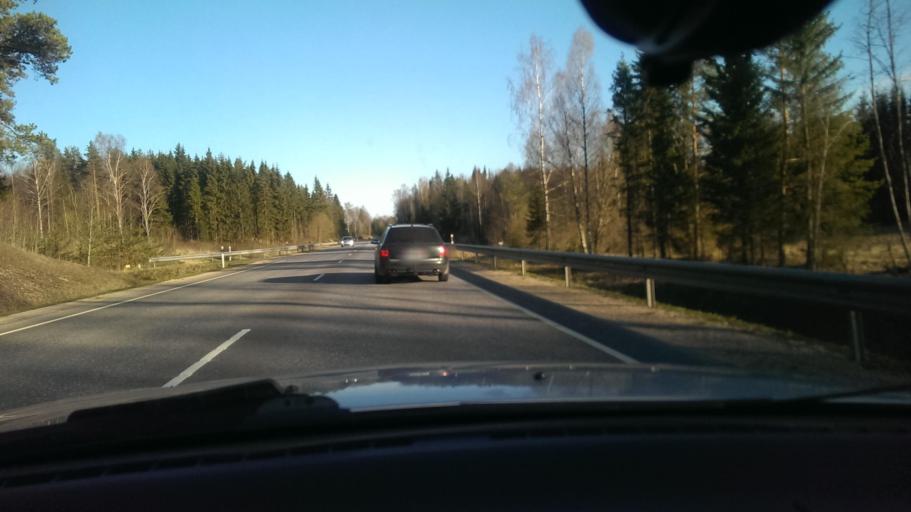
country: EE
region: Tartu
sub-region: UElenurme vald
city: Ulenurme
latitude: 58.1334
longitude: 26.7200
